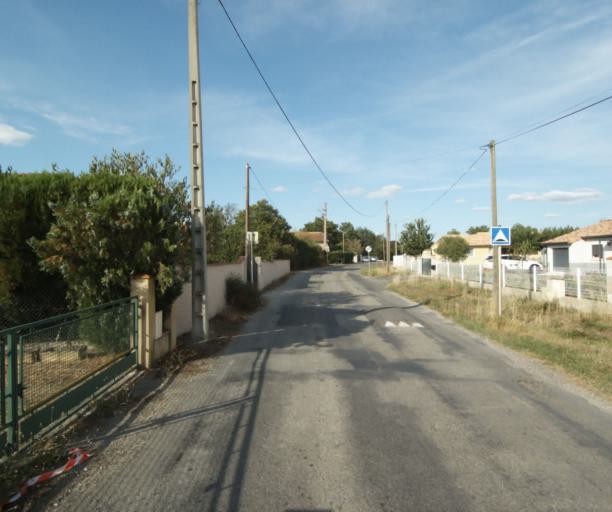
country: FR
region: Midi-Pyrenees
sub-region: Departement de la Haute-Garonne
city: Revel
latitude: 43.4634
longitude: 1.9867
